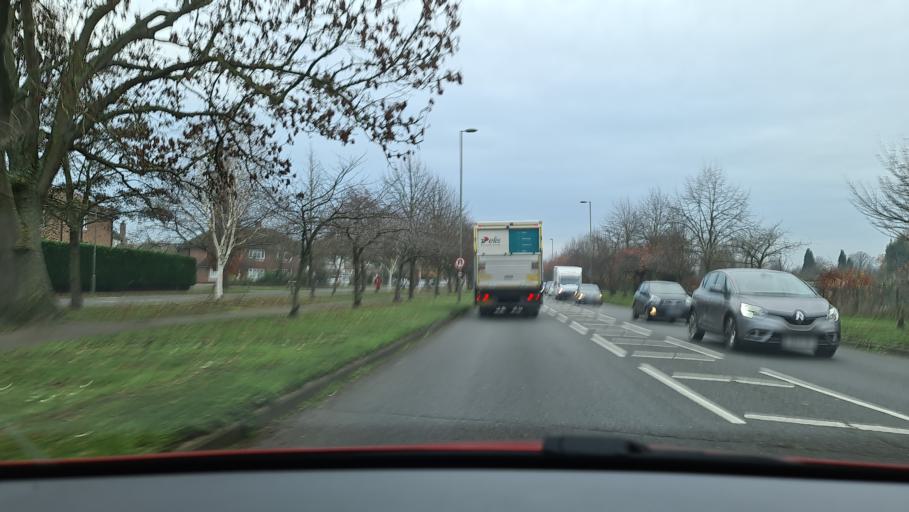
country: GB
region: England
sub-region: Surrey
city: Thames Ditton
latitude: 51.3937
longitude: -0.3437
